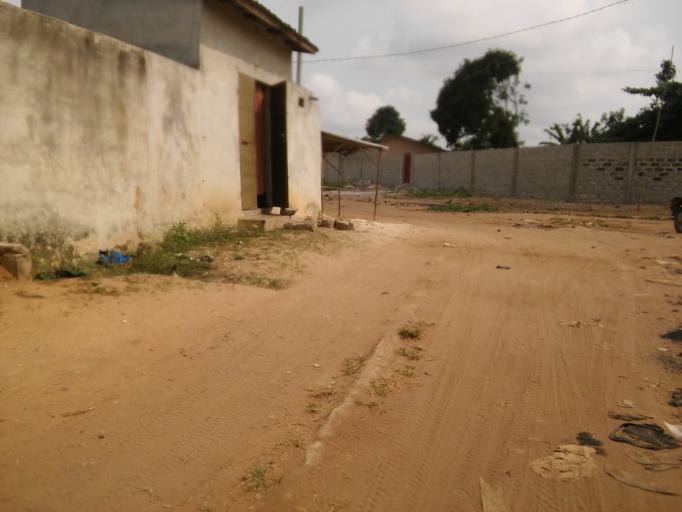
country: BJ
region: Atlantique
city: Abomey-Calavi
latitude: 6.4243
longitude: 2.3274
